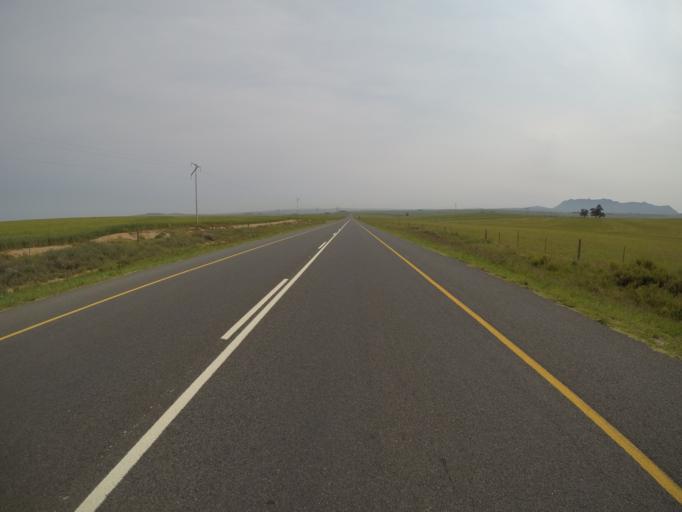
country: ZA
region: Western Cape
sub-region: West Coast District Municipality
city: Malmesbury
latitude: -33.5017
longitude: 18.8353
